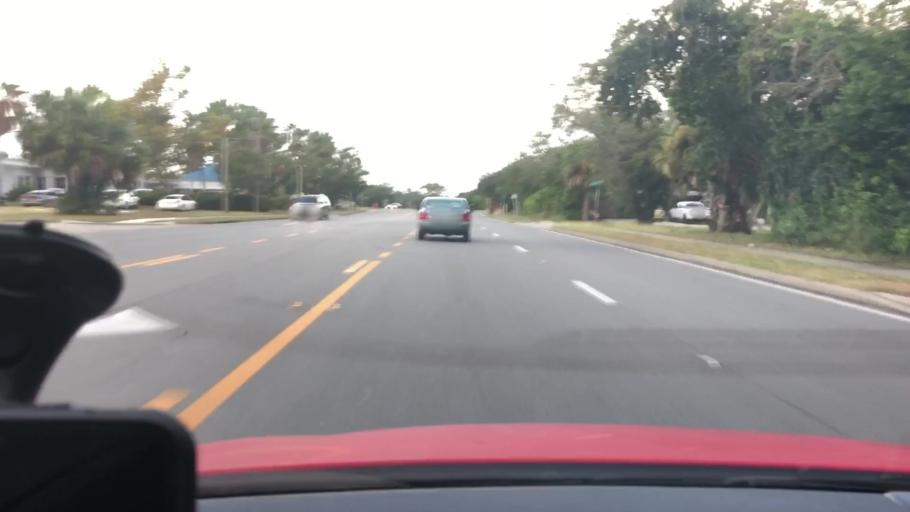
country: US
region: Florida
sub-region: Volusia County
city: Daytona Beach
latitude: 29.2077
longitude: -81.0538
